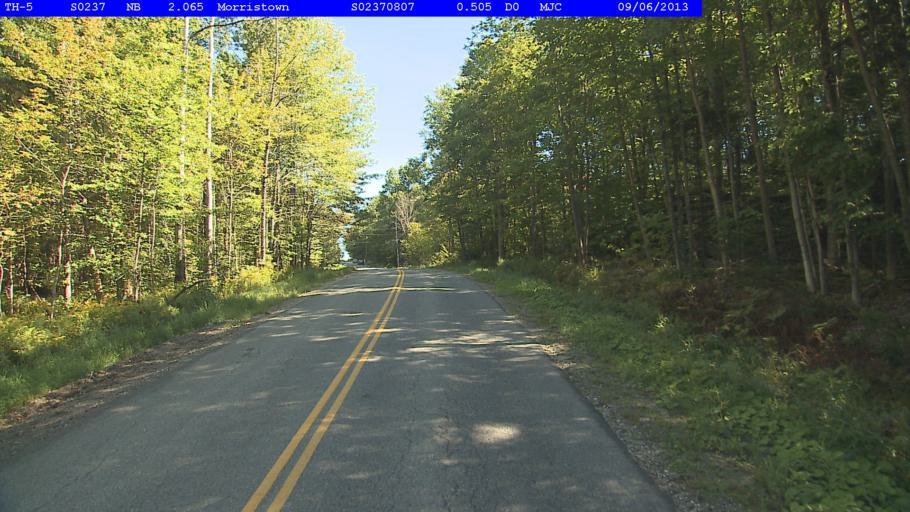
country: US
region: Vermont
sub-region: Lamoille County
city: Morristown
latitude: 44.5084
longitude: -72.6492
